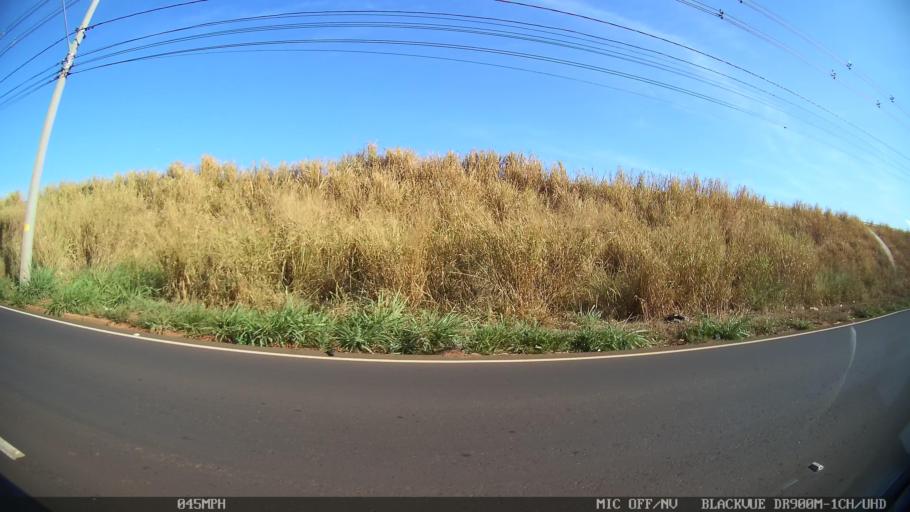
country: BR
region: Sao Paulo
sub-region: Sao Jose Do Rio Preto
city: Sao Jose do Rio Preto
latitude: -20.7621
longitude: -49.3460
